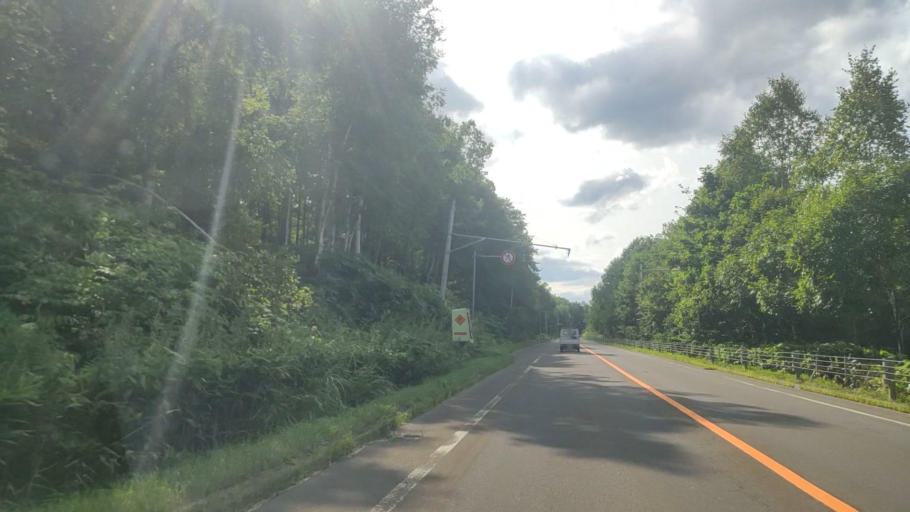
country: JP
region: Hokkaido
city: Nayoro
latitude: 44.3854
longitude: 142.4052
